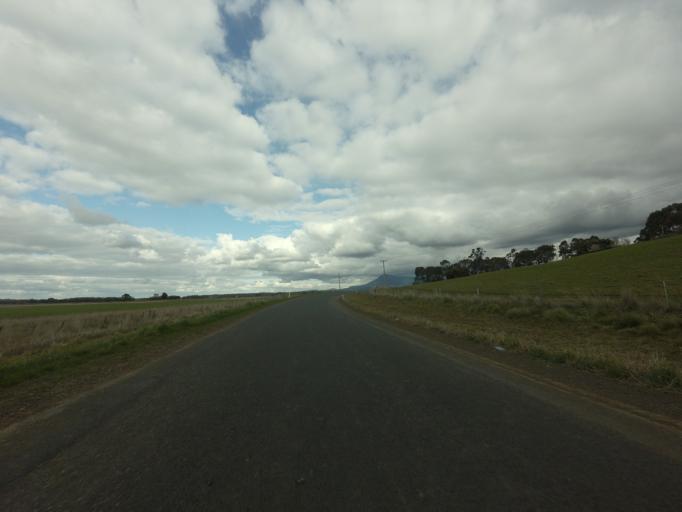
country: AU
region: Tasmania
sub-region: Northern Midlands
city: Longford
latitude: -41.7769
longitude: 147.0956
